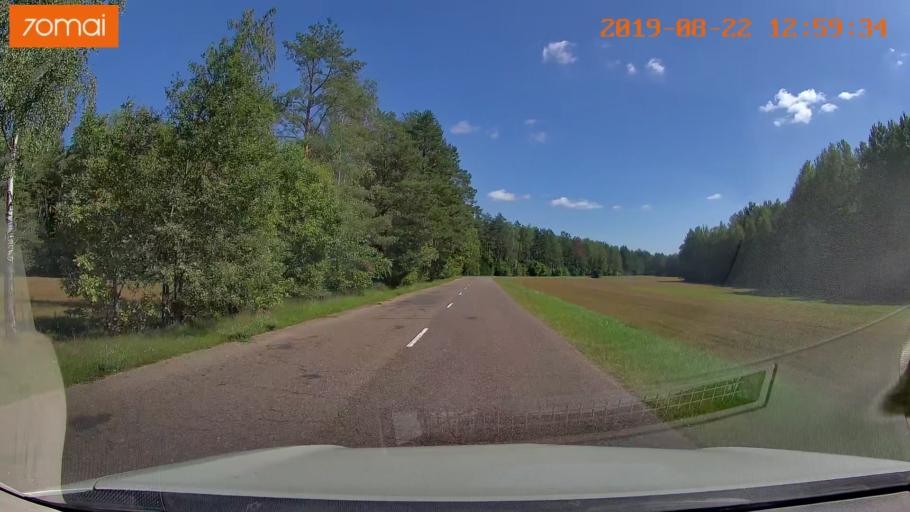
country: BY
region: Minsk
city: Prawdzinski
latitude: 53.4226
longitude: 27.7933
